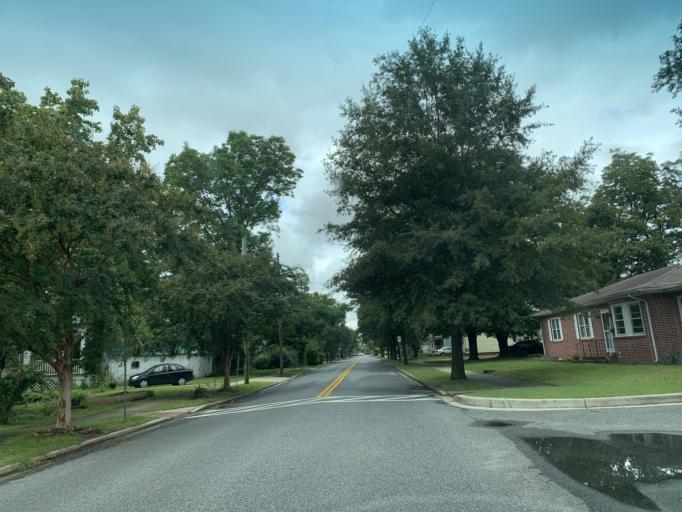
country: US
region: Maryland
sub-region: Caroline County
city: Denton
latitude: 38.8817
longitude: -75.8287
